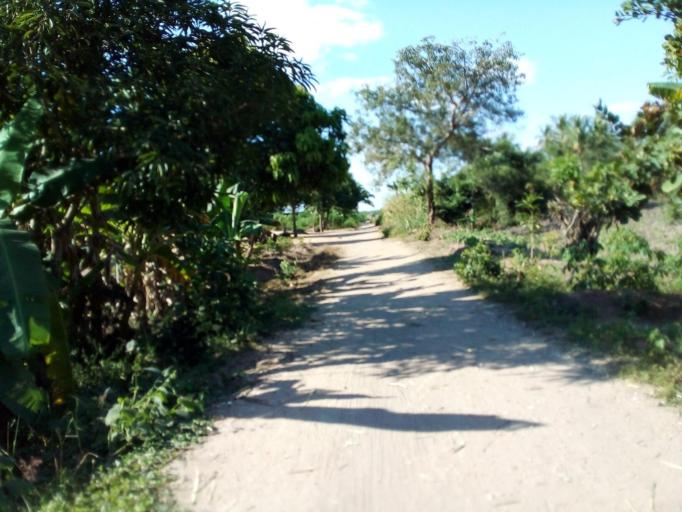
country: MZ
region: Zambezia
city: Quelimane
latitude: -17.5927
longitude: 36.8332
